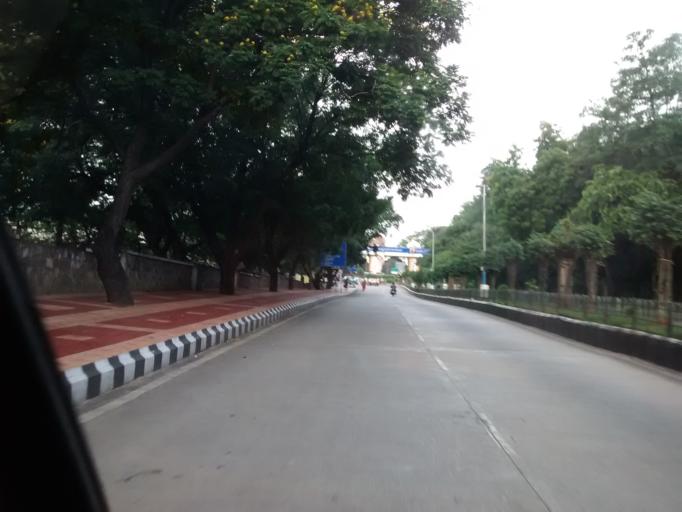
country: IN
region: Andhra Pradesh
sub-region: Chittoor
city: Akkarampalle
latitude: 13.6477
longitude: 79.4075
